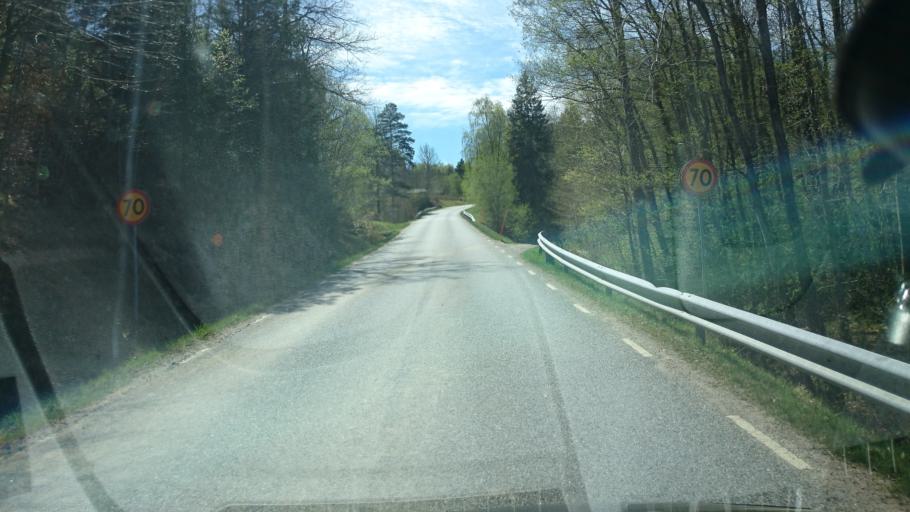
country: SE
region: Vaestra Goetaland
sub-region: Munkedals Kommun
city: Munkedal
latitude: 58.4250
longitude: 11.6941
